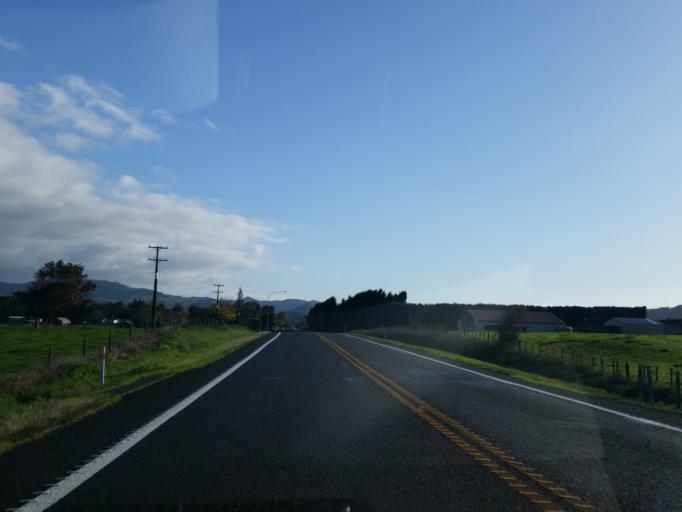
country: NZ
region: Waikato
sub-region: Hauraki District
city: Waihi
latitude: -37.4313
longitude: 175.8719
